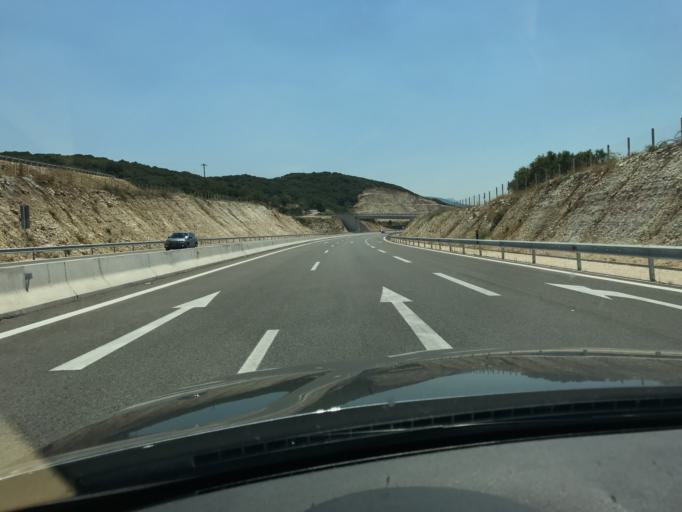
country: GR
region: Epirus
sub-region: Nomos Ioanninon
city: Agia Kyriaki
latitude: 39.4700
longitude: 20.8968
